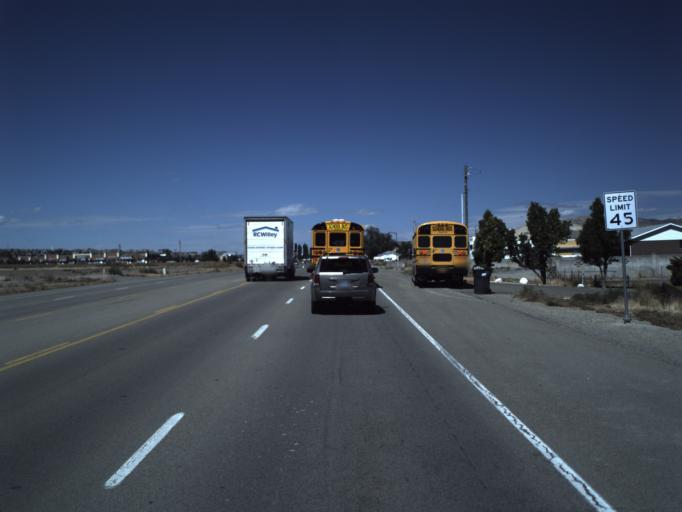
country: US
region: Utah
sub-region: Utah County
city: Saratoga Springs
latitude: 40.3800
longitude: -111.9163
